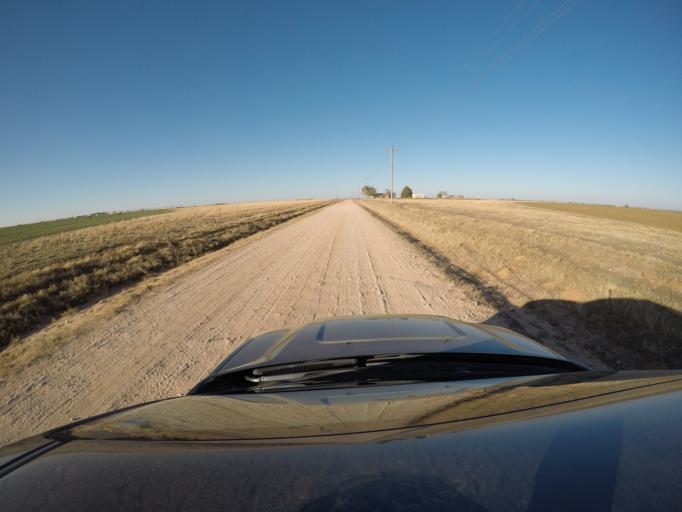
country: US
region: New Mexico
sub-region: Curry County
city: Texico
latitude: 34.3802
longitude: -103.1082
